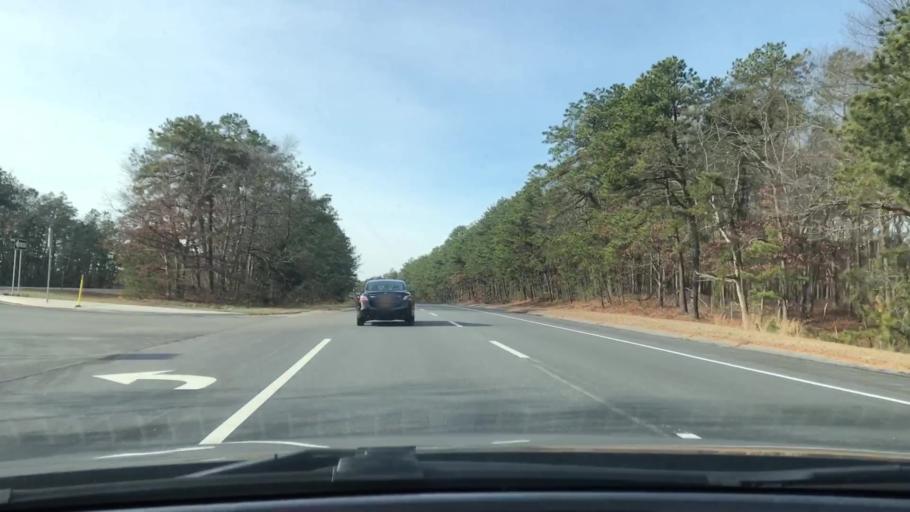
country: US
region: New York
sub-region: Suffolk County
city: Calverton
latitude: 40.9050
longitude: -72.7247
